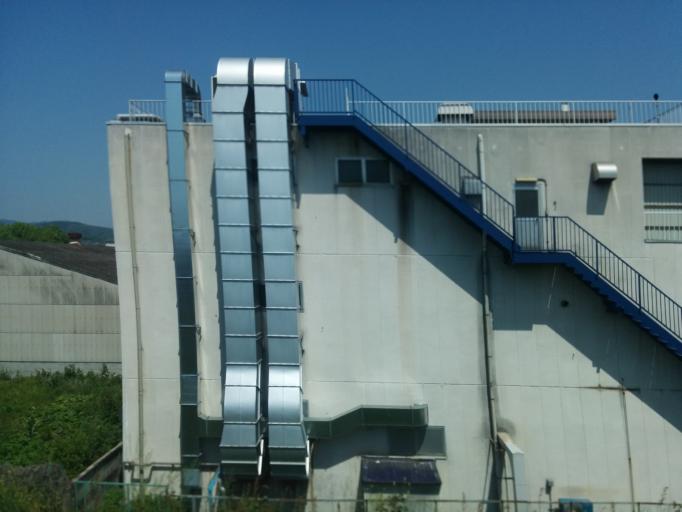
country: JP
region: Osaka
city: Takatsuki
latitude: 34.8446
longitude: 135.6120
